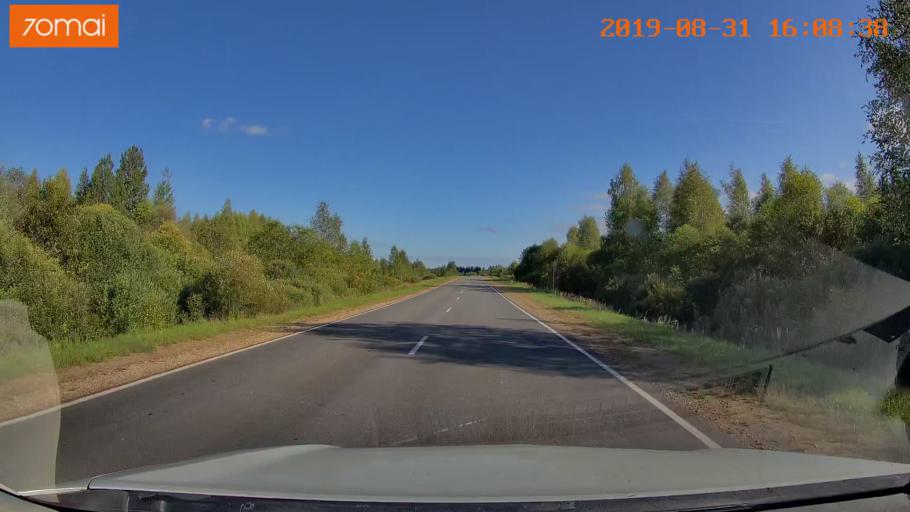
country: RU
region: Kaluga
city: Yukhnov
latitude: 54.5945
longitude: 35.3797
